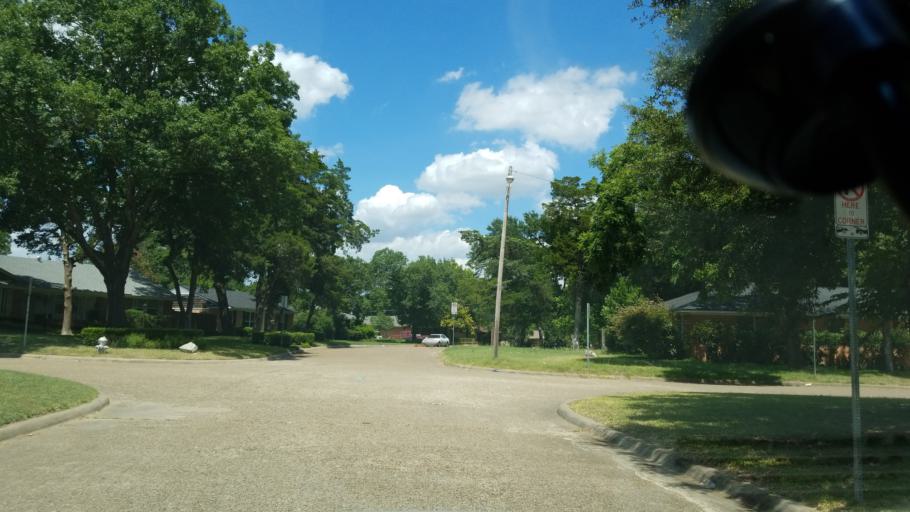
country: US
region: Texas
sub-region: Dallas County
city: Cockrell Hill
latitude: 32.7025
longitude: -96.8732
